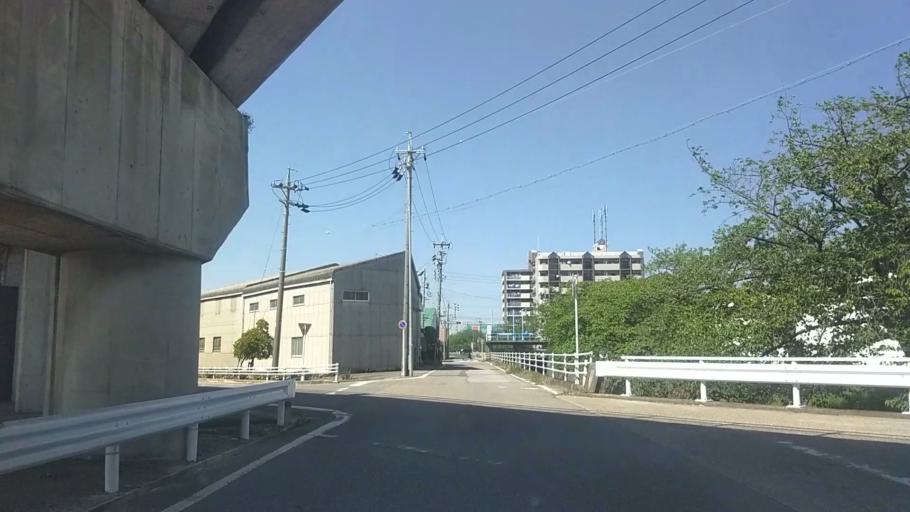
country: JP
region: Aichi
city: Okazaki
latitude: 34.9786
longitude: 137.1574
